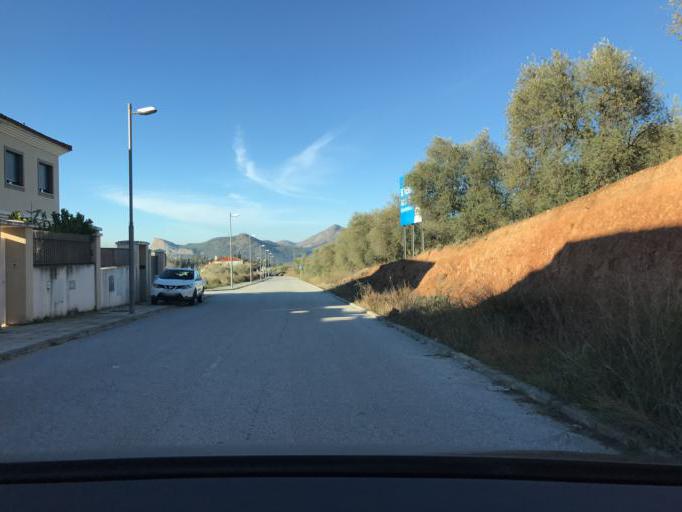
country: ES
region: Andalusia
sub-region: Provincia de Granada
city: Peligros
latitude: 37.2555
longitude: -3.6408
